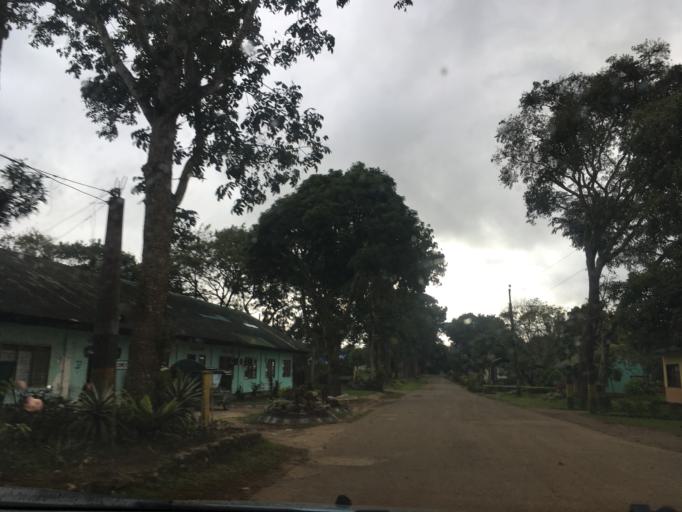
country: PH
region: Calabarzon
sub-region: Province of Rizal
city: Sampaloc
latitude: 14.5385
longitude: 121.3651
